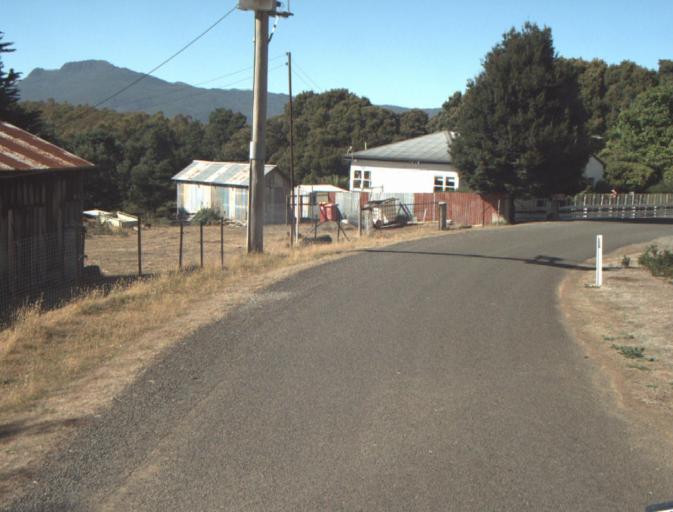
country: AU
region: Tasmania
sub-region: Dorset
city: Scottsdale
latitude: -41.2886
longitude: 147.3602
